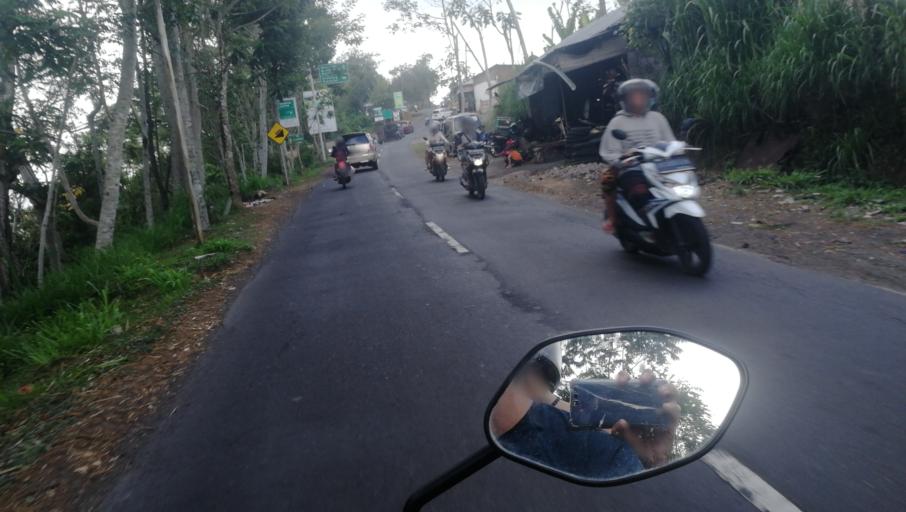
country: ID
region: Bali
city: Munduk
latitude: -8.2499
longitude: 115.0947
